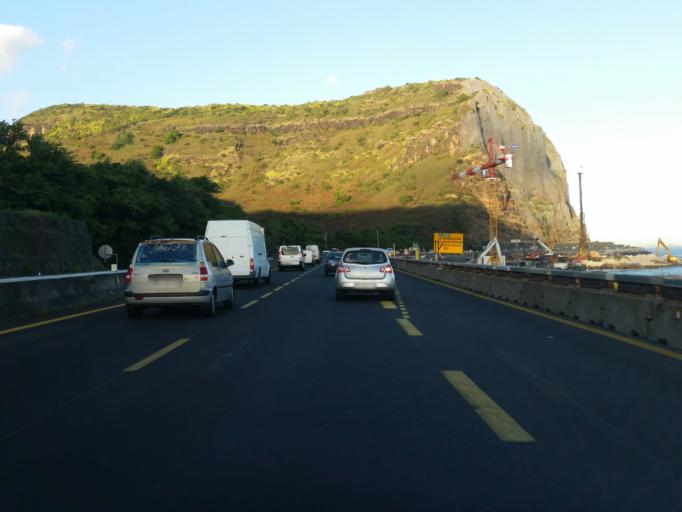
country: RE
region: Reunion
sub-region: Reunion
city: La Possession
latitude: -20.8942
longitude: 55.3781
